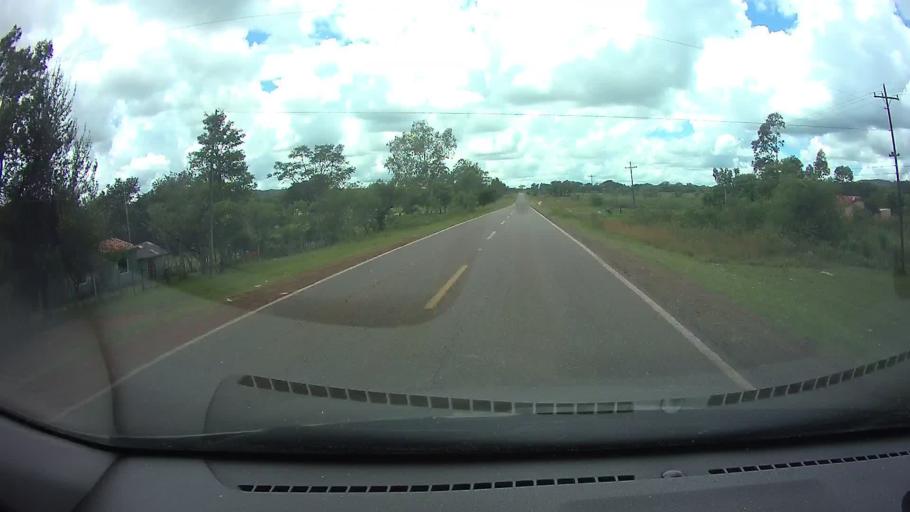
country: PY
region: Paraguari
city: La Colmena
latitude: -25.8971
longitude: -56.9591
